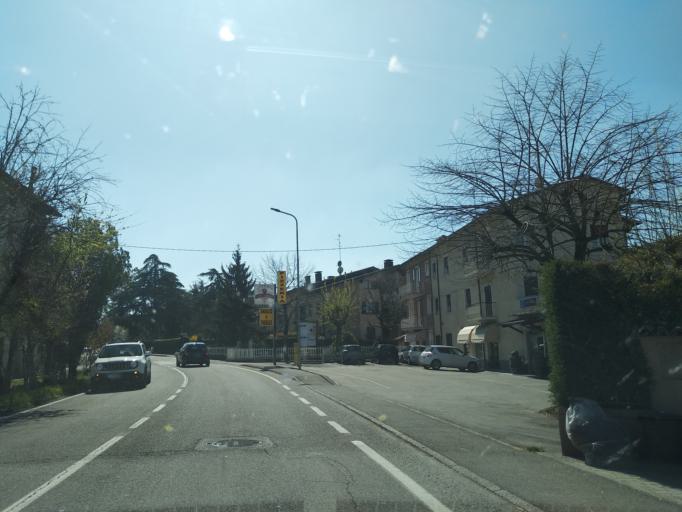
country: IT
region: Emilia-Romagna
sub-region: Provincia di Reggio Emilia
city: Albinea
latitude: 44.6339
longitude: 10.6052
